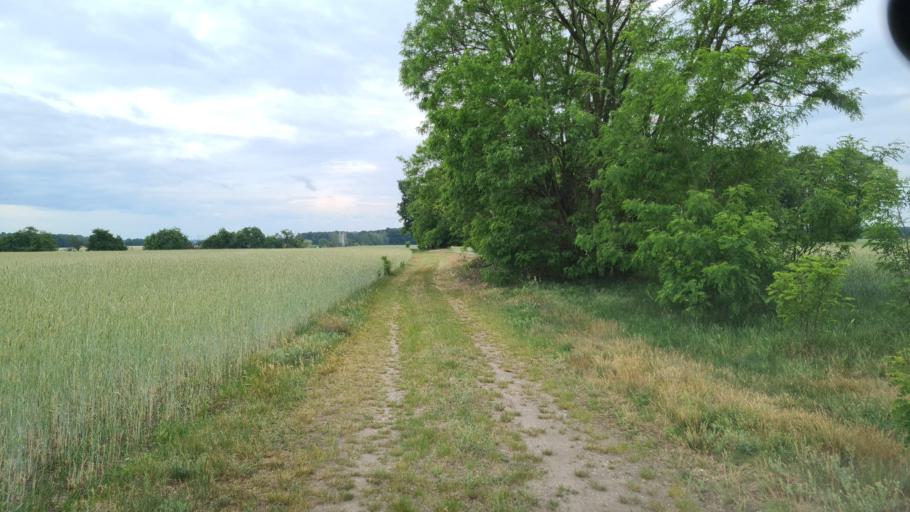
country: DE
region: Brandenburg
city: Bronkow
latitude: 51.6256
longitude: 13.9371
